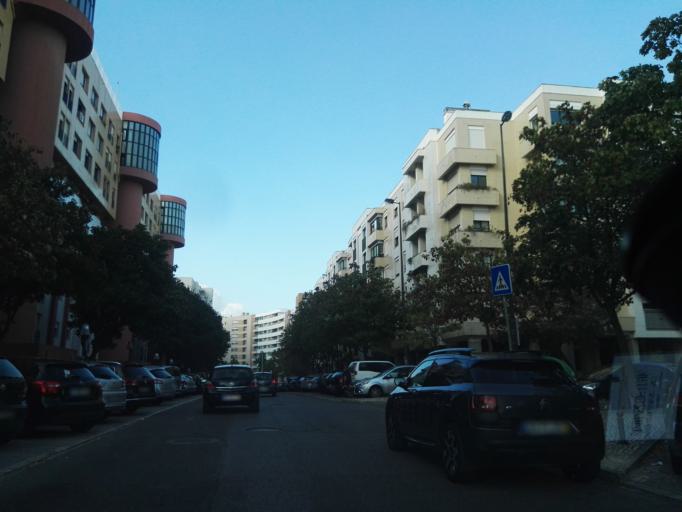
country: PT
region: Lisbon
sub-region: Odivelas
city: Olival do Basto
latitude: 38.7654
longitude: -9.1526
